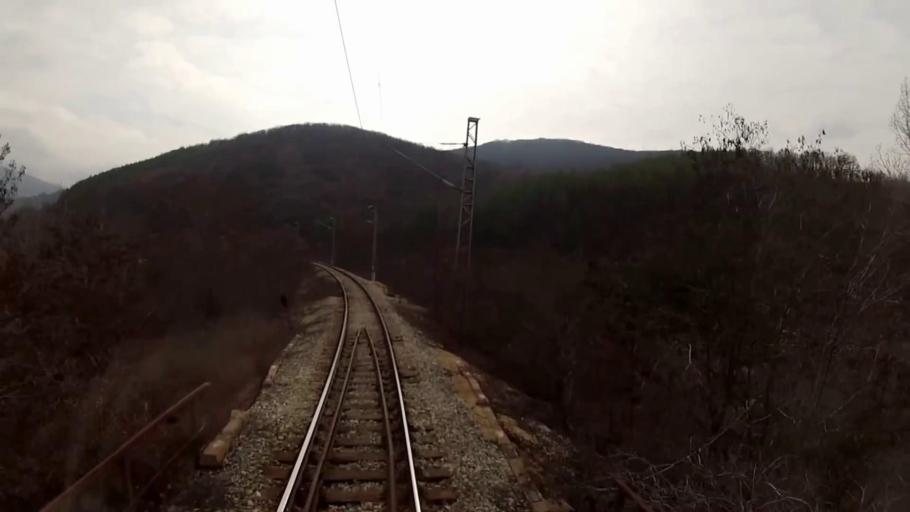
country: BG
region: Sofiya
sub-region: Obshtina Gorna Malina
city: Gorna Malina
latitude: 42.6893
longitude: 23.8045
